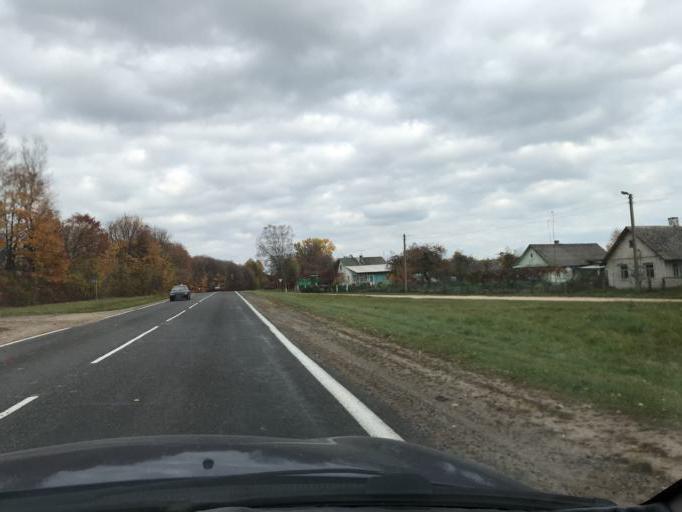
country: BY
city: Berezovka
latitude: 53.7455
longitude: 25.3774
